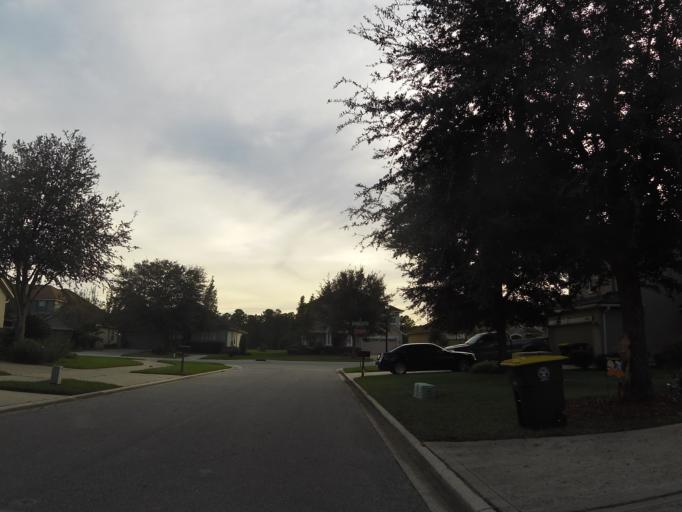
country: US
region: Florida
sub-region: Saint Johns County
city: Fruit Cove
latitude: 30.1498
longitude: -81.5426
